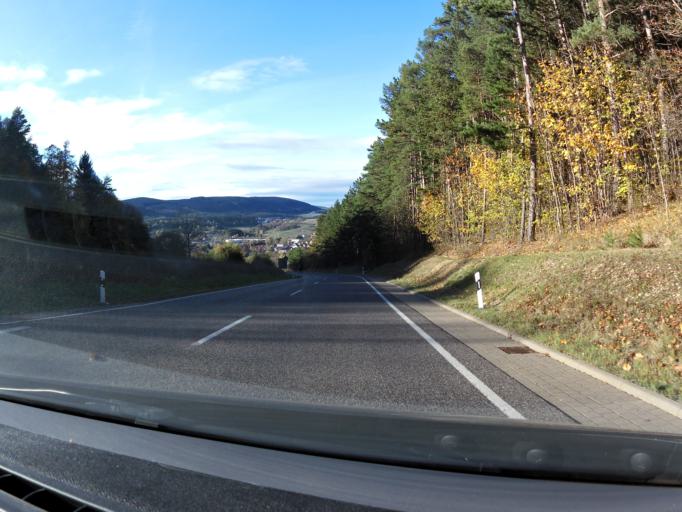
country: DE
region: Thuringia
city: Geschwenda
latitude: 50.7408
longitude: 10.8239
